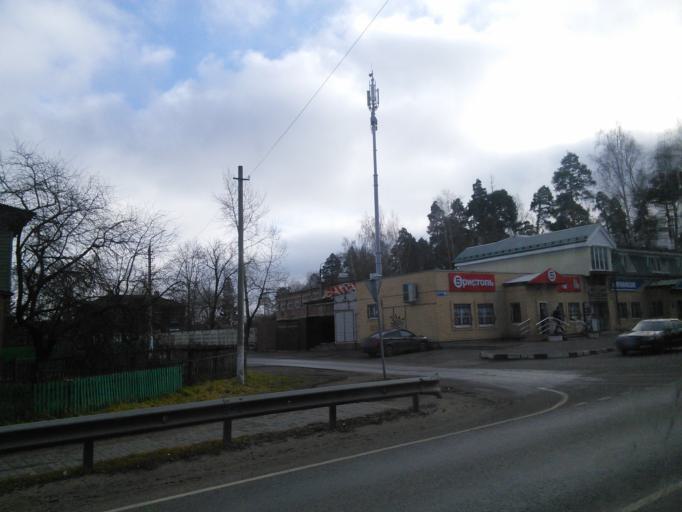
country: RU
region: Moskovskaya
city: Likino-Dulevo
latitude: 55.7086
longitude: 38.9578
